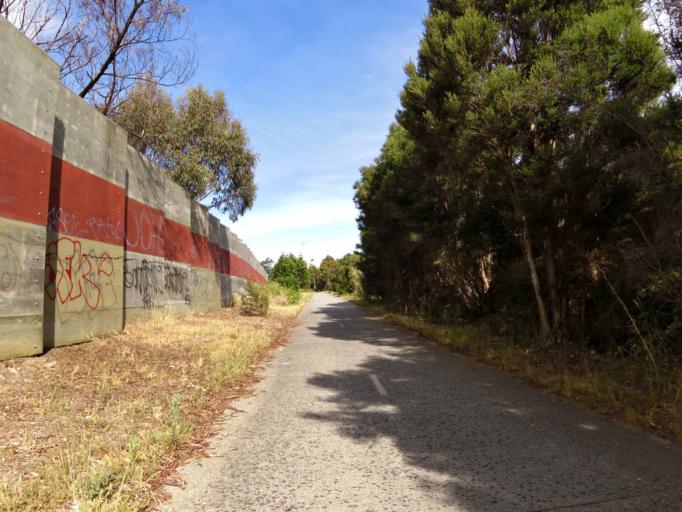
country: AU
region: Victoria
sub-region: Casey
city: Hallam
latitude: -37.9980
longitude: 145.2726
